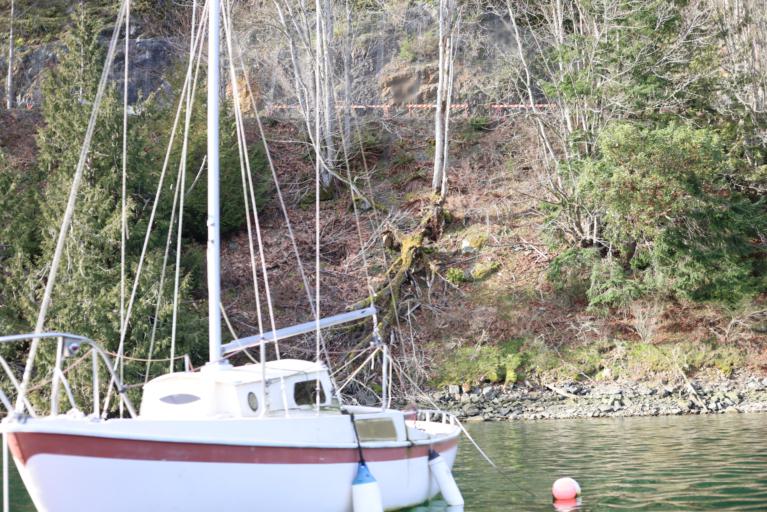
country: CA
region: British Columbia
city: Duncan
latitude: 48.7606
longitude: -123.6000
